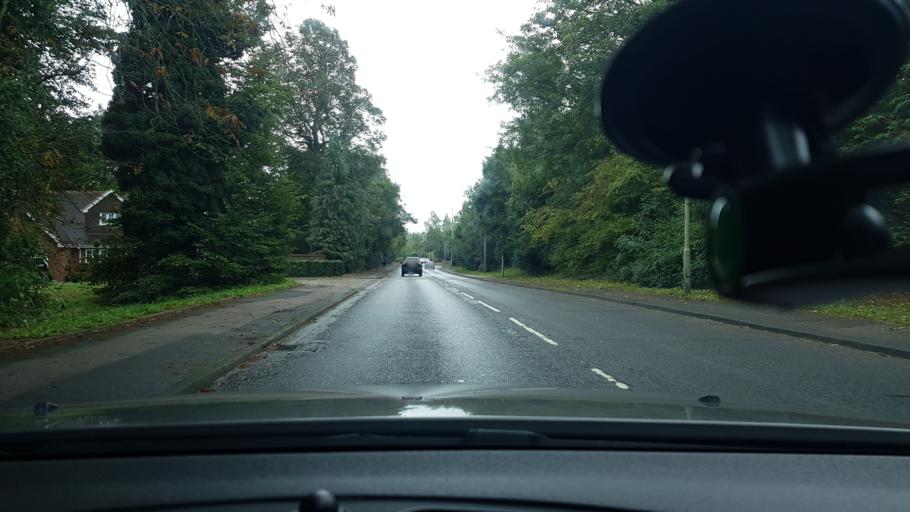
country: GB
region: England
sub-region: Hertfordshire
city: Chorleywood
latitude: 51.6520
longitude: -0.4840
